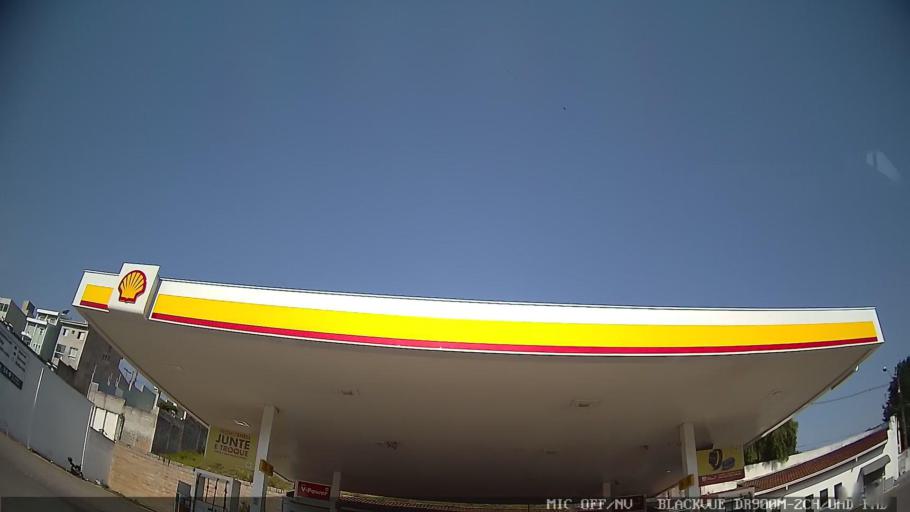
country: BR
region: Sao Paulo
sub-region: Itatiba
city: Itatiba
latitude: -22.9980
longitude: -46.8482
